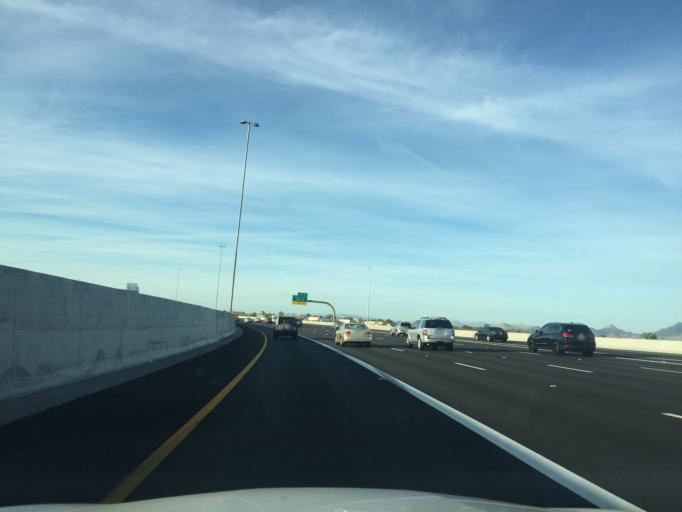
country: US
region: Arizona
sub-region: Maricopa County
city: Scottsdale
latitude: 33.5577
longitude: -111.8796
